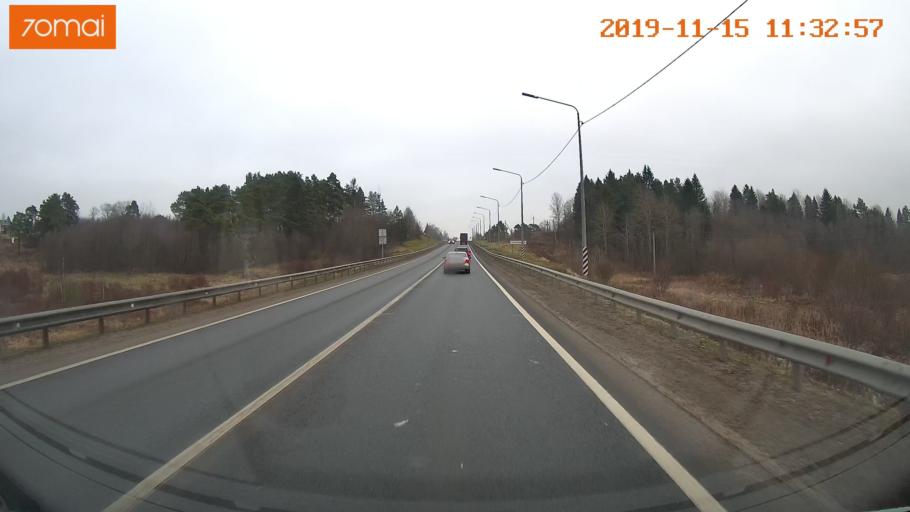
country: RU
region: Vologda
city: Molochnoye
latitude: 59.1876
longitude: 39.5839
